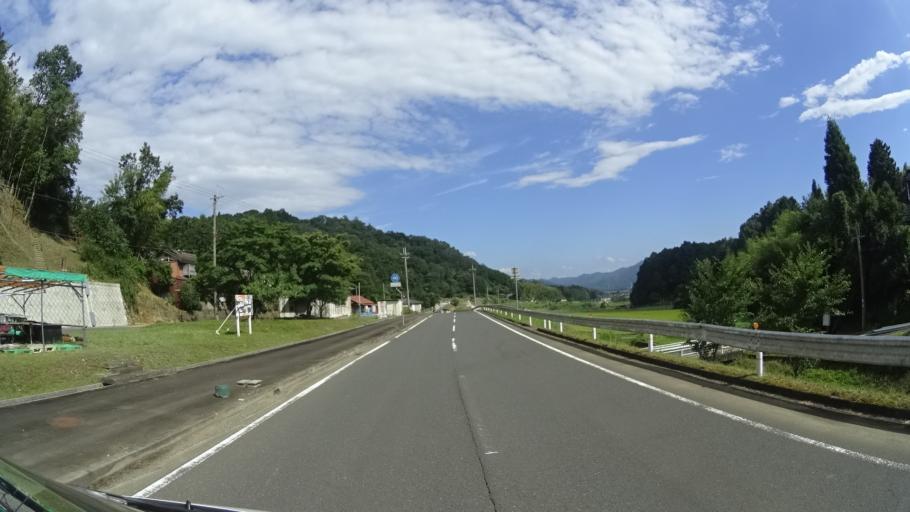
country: JP
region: Kyoto
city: Fukuchiyama
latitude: 35.3406
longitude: 135.1663
